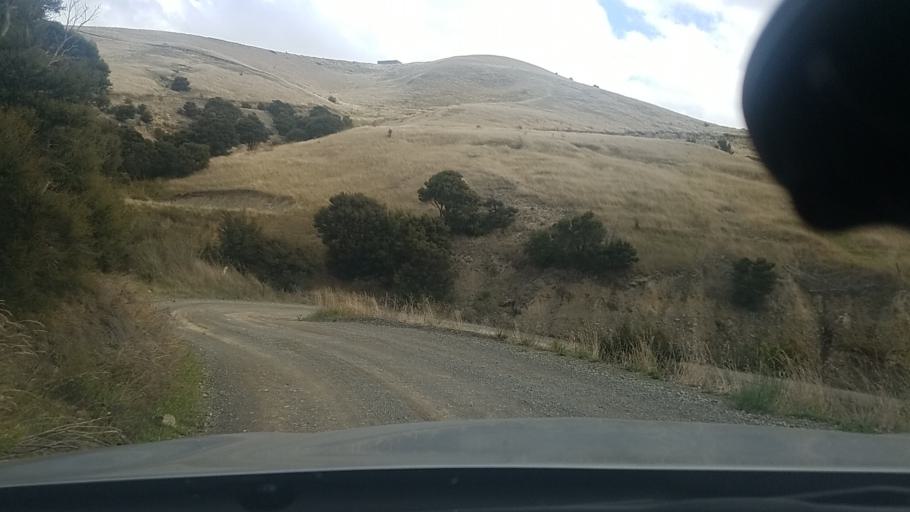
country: NZ
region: Marlborough
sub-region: Marlborough District
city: Blenheim
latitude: -41.5859
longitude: 174.0744
